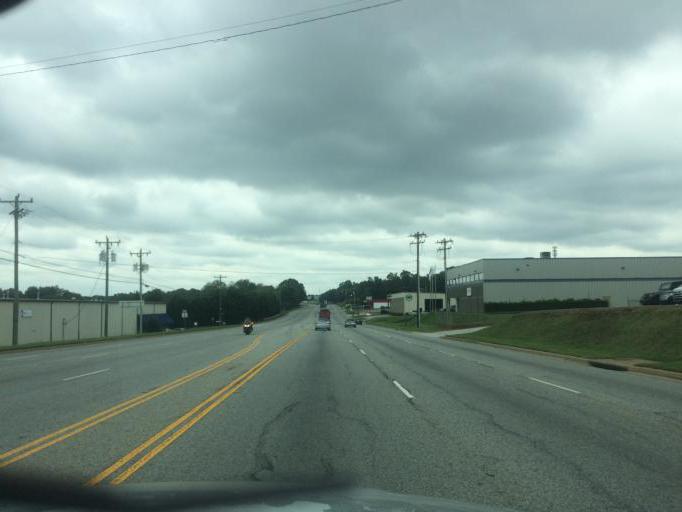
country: US
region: South Carolina
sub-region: Greenville County
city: Greer
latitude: 34.8938
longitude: -82.2338
